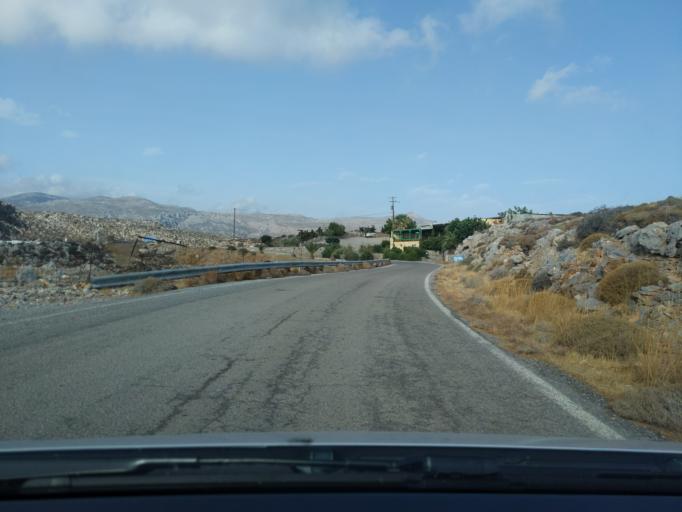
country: GR
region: Crete
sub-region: Nomos Lasithiou
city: Palekastro
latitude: 35.0849
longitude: 26.2569
